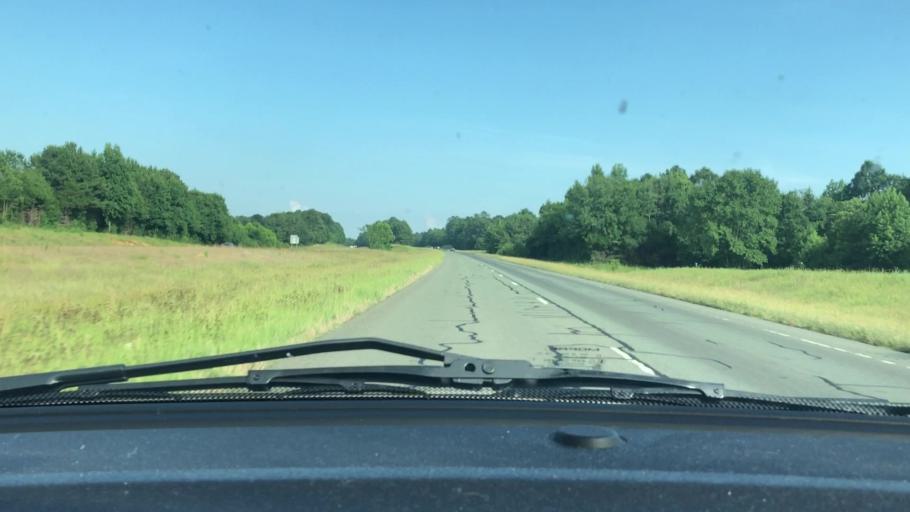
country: US
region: North Carolina
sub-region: Randolph County
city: Liberty
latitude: 35.7930
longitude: -79.5300
